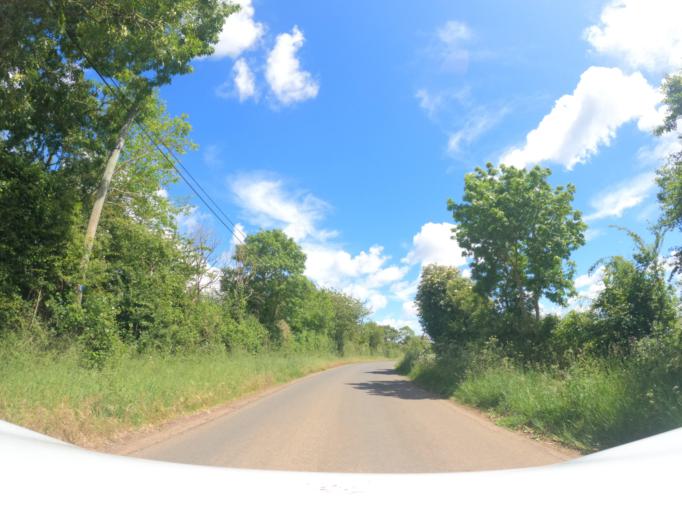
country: FR
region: Pays de la Loire
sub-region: Departement de la Vendee
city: Le Champ-Saint-Pere
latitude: 46.4938
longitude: -1.3389
